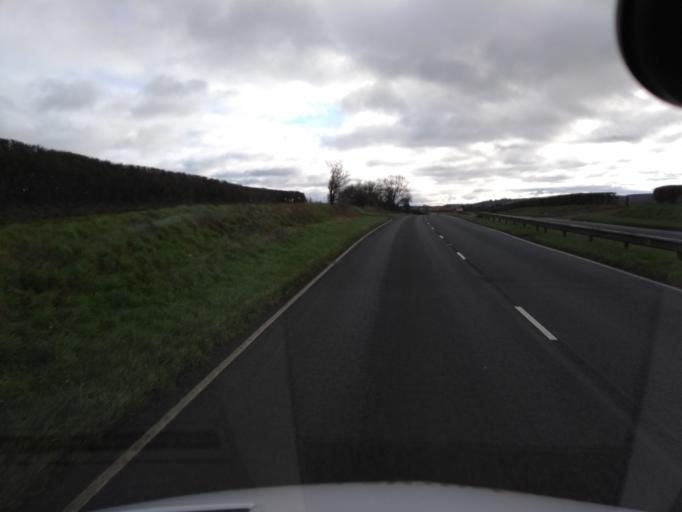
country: GB
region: England
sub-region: Dorset
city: Sherborne
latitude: 50.9461
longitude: -2.5492
